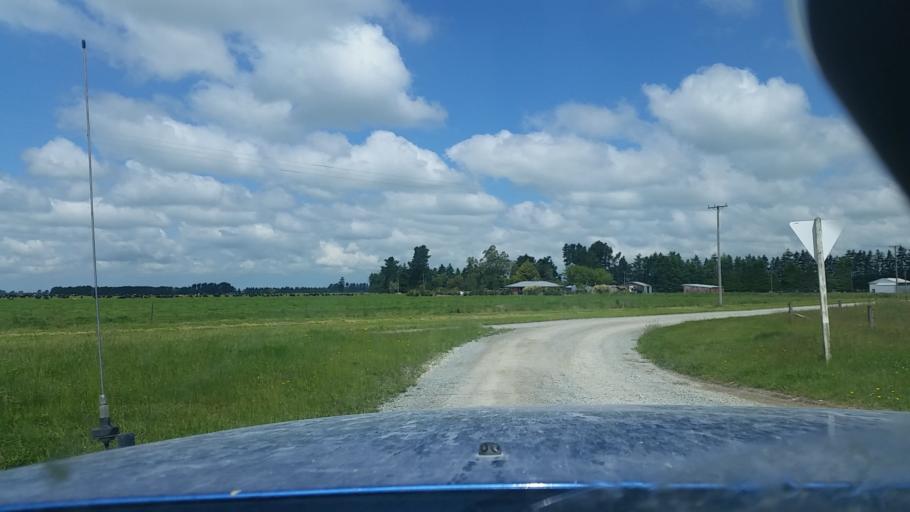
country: NZ
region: Canterbury
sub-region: Ashburton District
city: Tinwald
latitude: -43.9102
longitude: 171.3771
